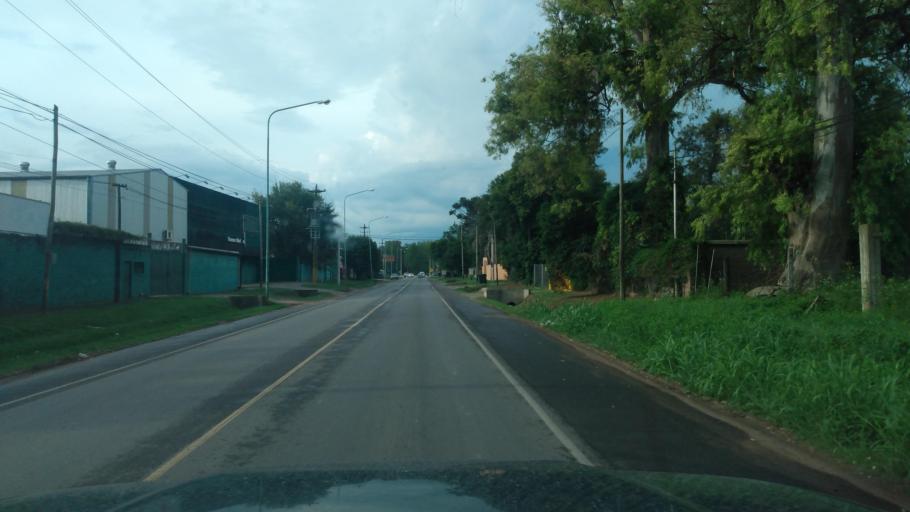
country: AR
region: Buenos Aires
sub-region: Partido de Lujan
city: Lujan
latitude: -34.5534
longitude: -59.1256
